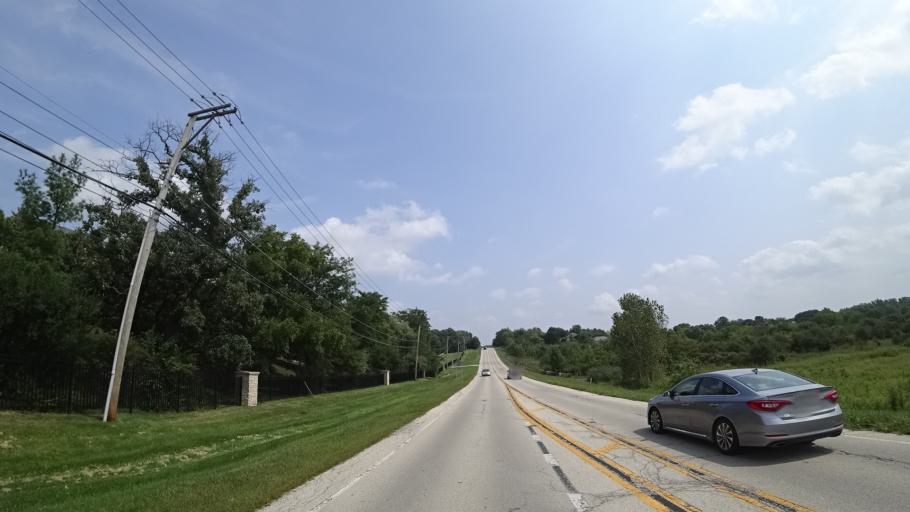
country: US
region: Illinois
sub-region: Will County
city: Goodings Grove
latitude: 41.6151
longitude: -87.8999
